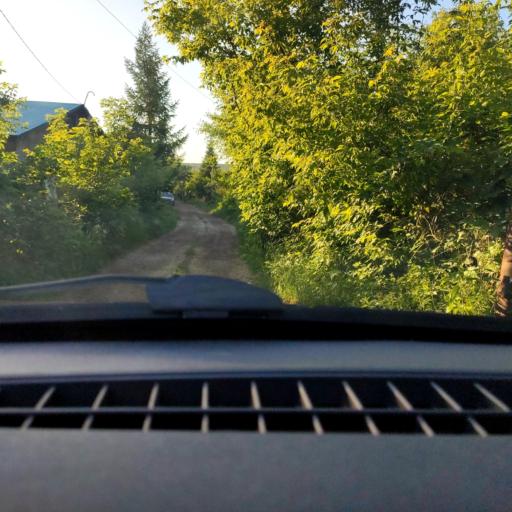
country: RU
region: Bashkortostan
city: Avdon
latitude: 54.6123
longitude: 55.6872
